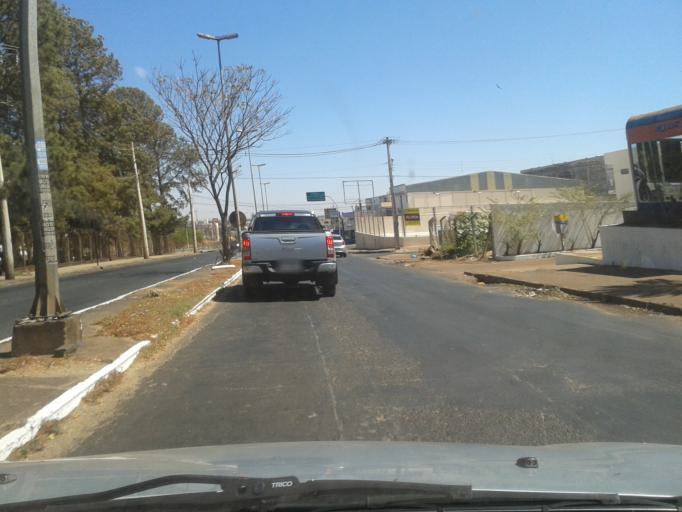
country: BR
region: Minas Gerais
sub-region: Uberlandia
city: Uberlandia
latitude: -18.8822
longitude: -48.2691
